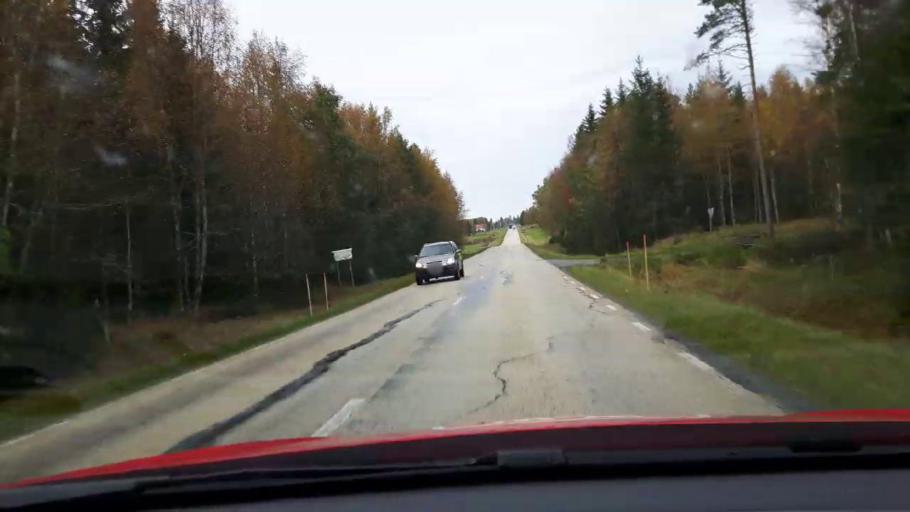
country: SE
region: Jaemtland
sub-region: Bergs Kommun
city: Hoverberg
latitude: 62.9307
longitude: 14.3350
